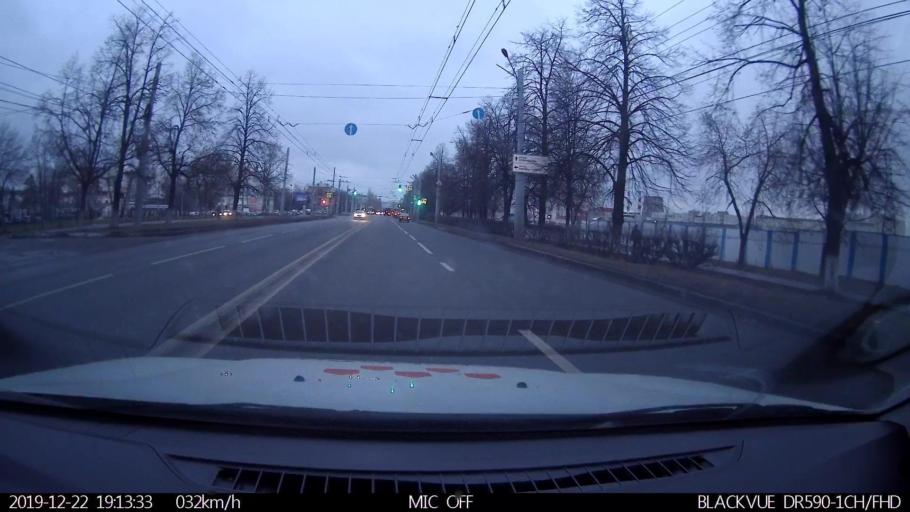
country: RU
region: Nizjnij Novgorod
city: Nizhniy Novgorod
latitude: 56.3298
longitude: 43.9029
